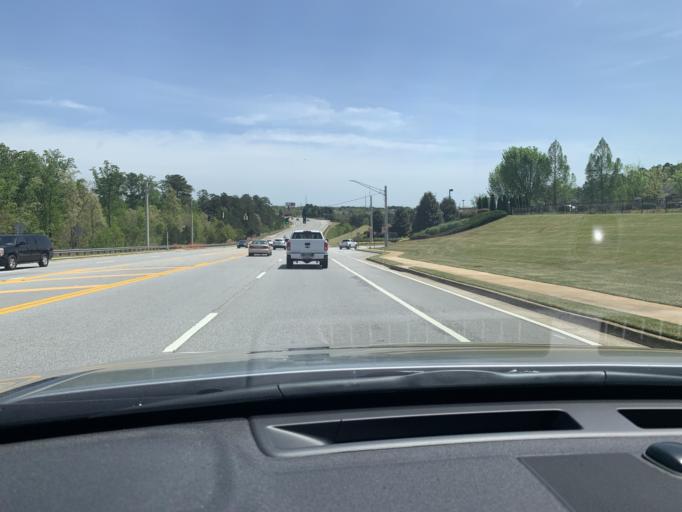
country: US
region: Georgia
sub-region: Oconee County
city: Watkinsville
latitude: 33.9177
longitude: -83.4537
